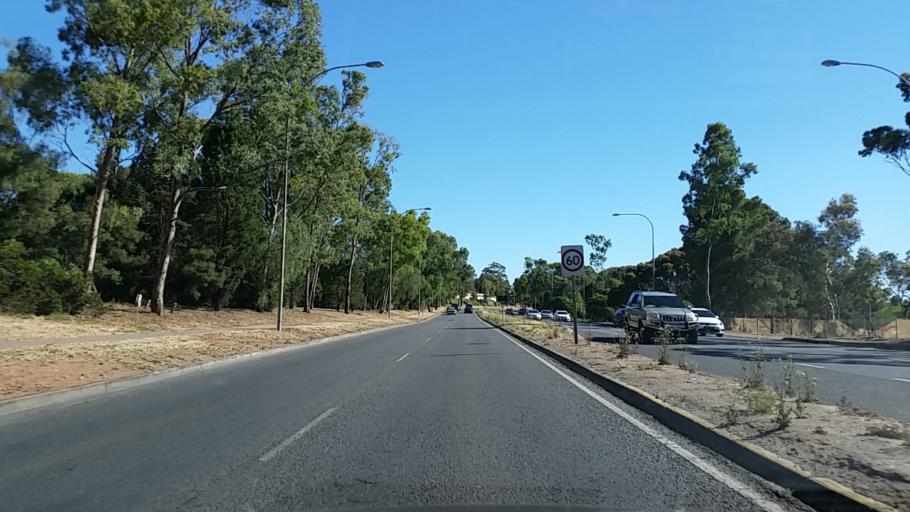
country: AU
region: South Australia
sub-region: Salisbury
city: Ingle Farm
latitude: -34.8161
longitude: 138.6415
